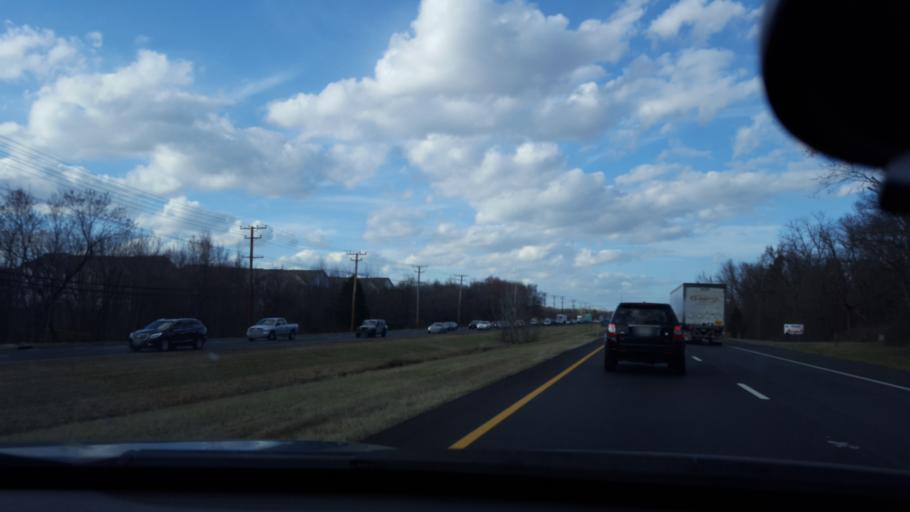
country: US
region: Maryland
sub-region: Prince George's County
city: Bowie
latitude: 38.9385
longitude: -76.7177
